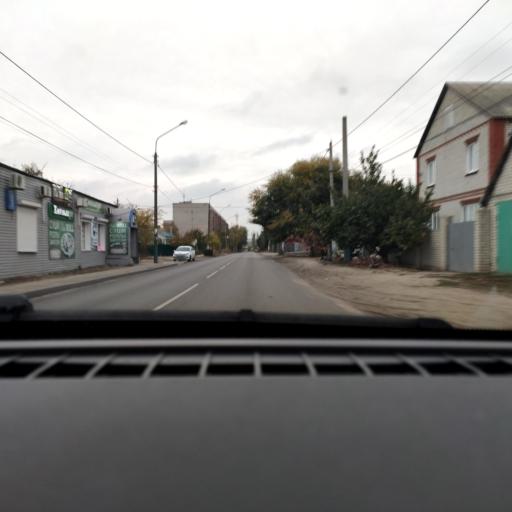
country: RU
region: Voronezj
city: Somovo
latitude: 51.7341
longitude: 39.2838
